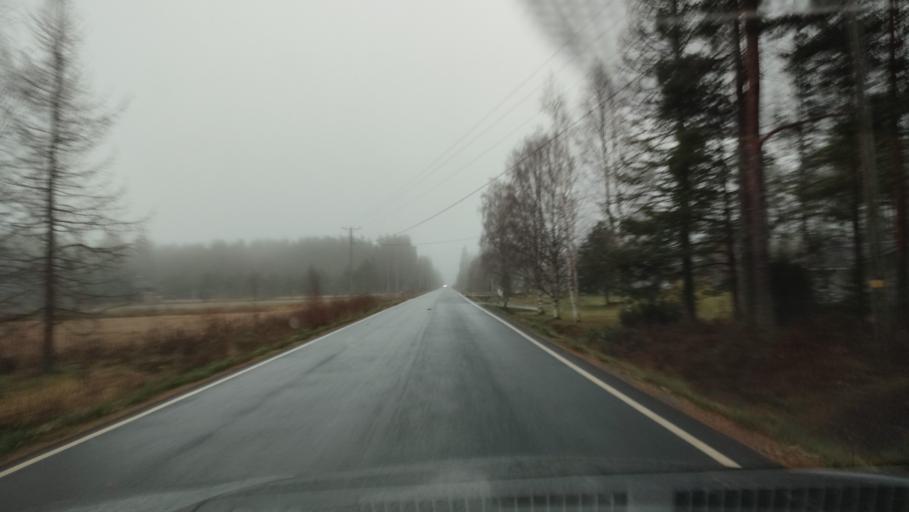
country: FI
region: Southern Ostrobothnia
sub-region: Suupohja
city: Karijoki
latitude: 62.1829
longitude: 21.7803
